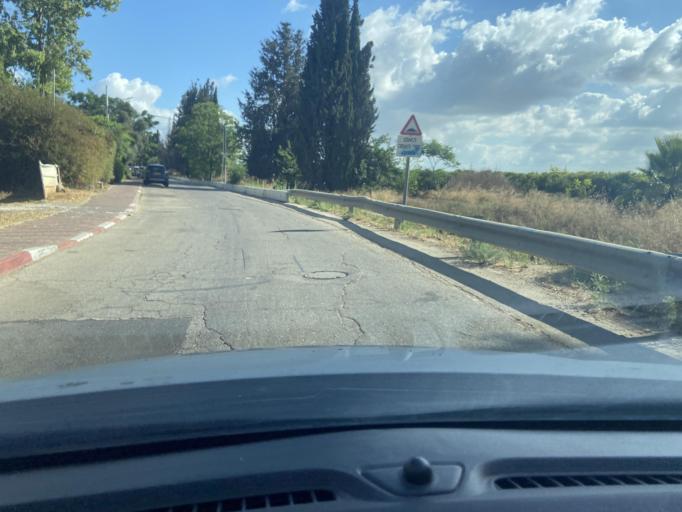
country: IL
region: Central District
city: Yehud
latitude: 32.0338
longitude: 34.8988
